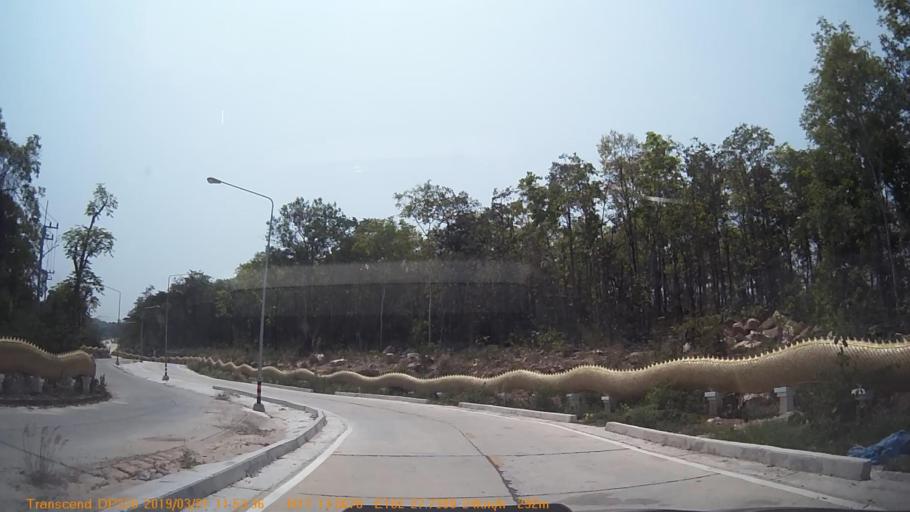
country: TH
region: Changwat Nong Bua Lamphu
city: Nong Bua Lamphu
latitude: 17.2260
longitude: 102.4623
